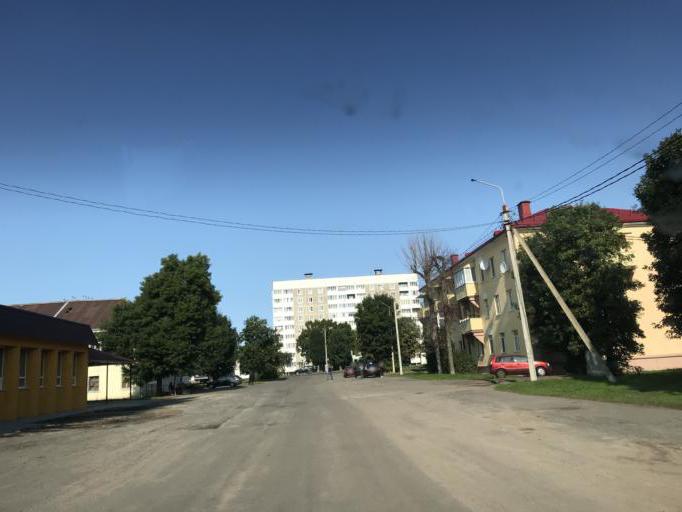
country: BY
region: Mogilev
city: Buynichy
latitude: 53.8815
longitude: 30.2708
